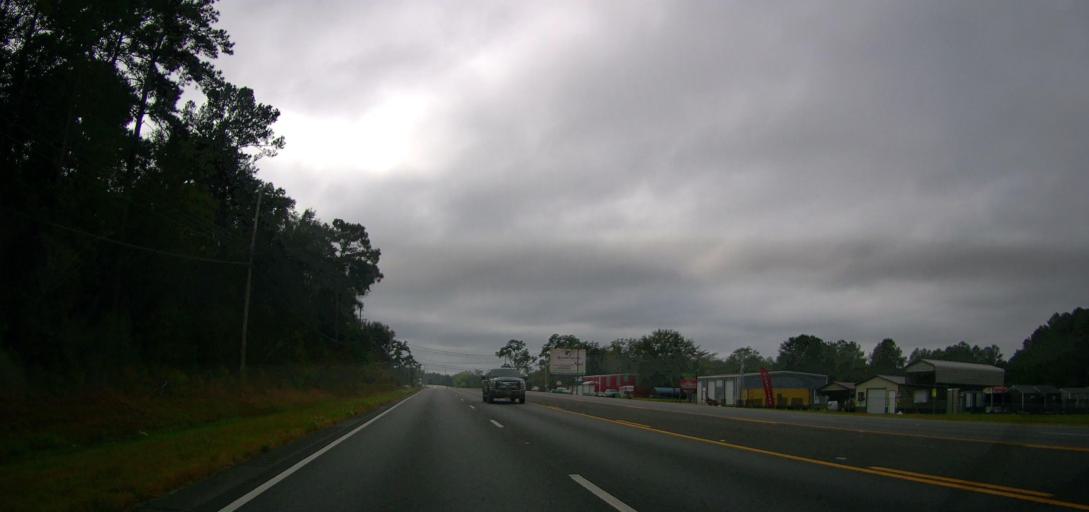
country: US
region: Georgia
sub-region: Thomas County
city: Thomasville
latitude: 30.8776
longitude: -83.9340
